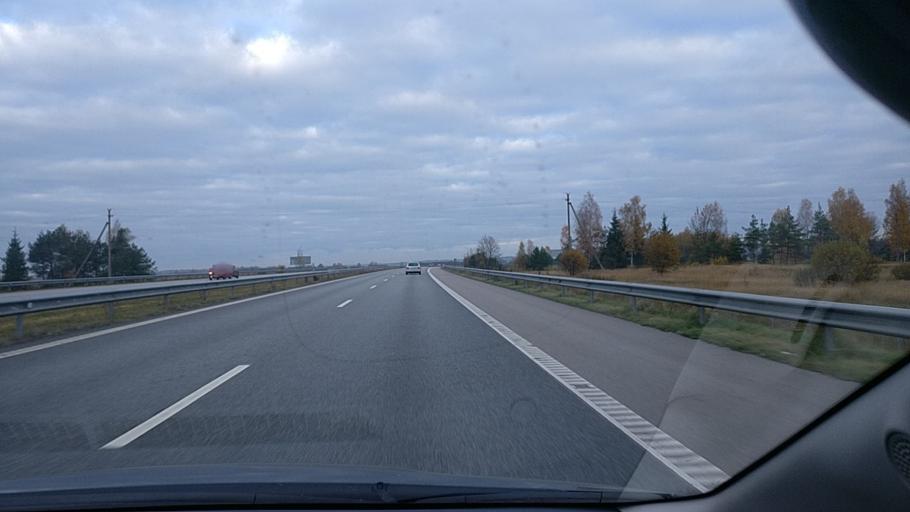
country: LT
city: Sirvintos
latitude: 54.9189
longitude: 24.9976
